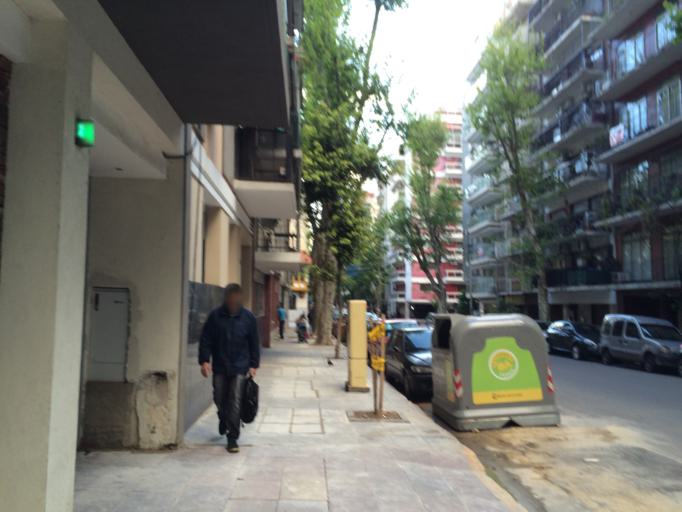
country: AR
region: Buenos Aires F.D.
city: Retiro
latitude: -34.5900
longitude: -58.4026
